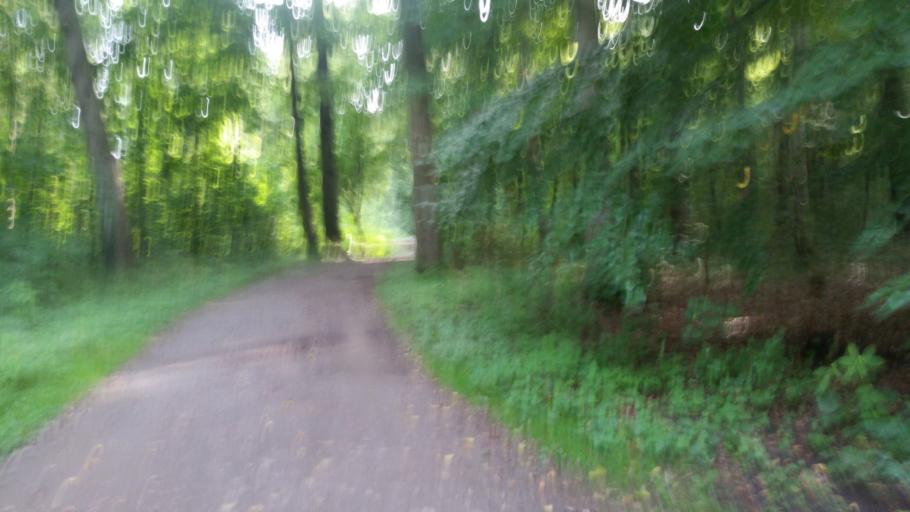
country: DE
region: Lower Saxony
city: Hannover
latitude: 52.3914
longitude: 9.7693
